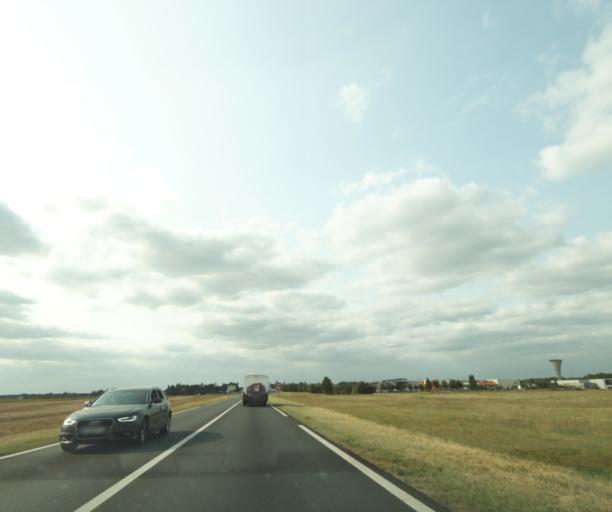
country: FR
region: Centre
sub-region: Departement d'Indre-et-Loire
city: Esvres
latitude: 47.2956
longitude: 0.8039
